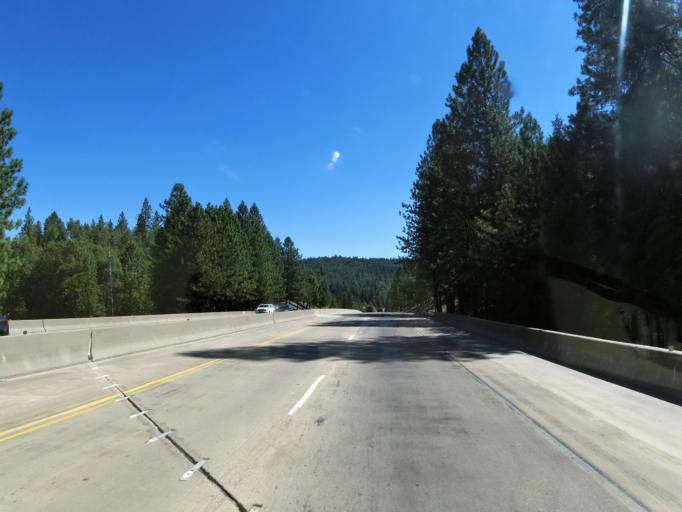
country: US
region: California
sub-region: Placer County
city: Colfax
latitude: 39.1545
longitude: -120.8882
